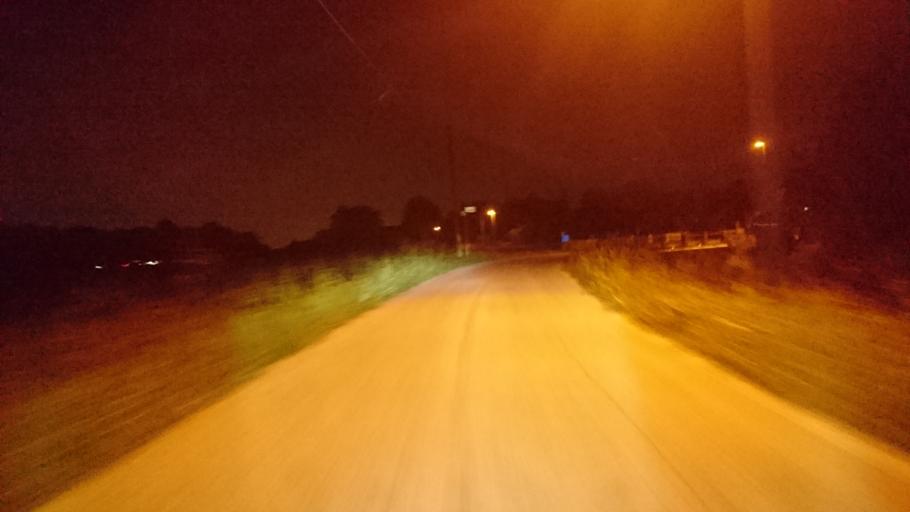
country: IT
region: Veneto
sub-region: Provincia di Padova
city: Terradura
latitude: 45.3318
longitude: 11.8125
